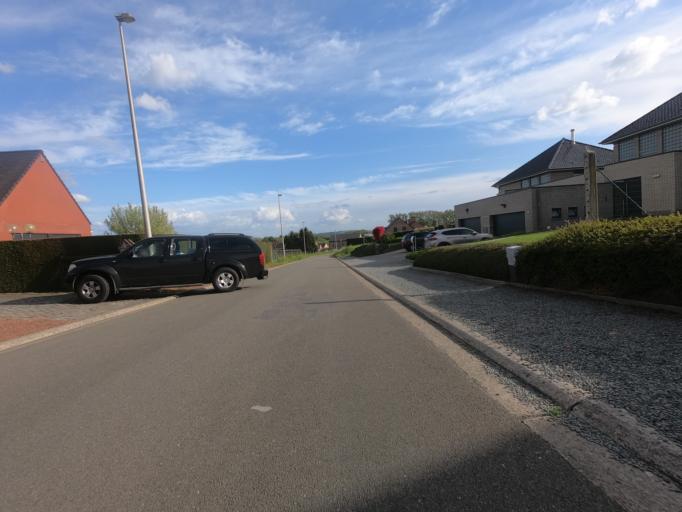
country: BE
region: Flanders
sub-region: Provincie Oost-Vlaanderen
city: Herzele
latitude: 50.8296
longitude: 3.9384
